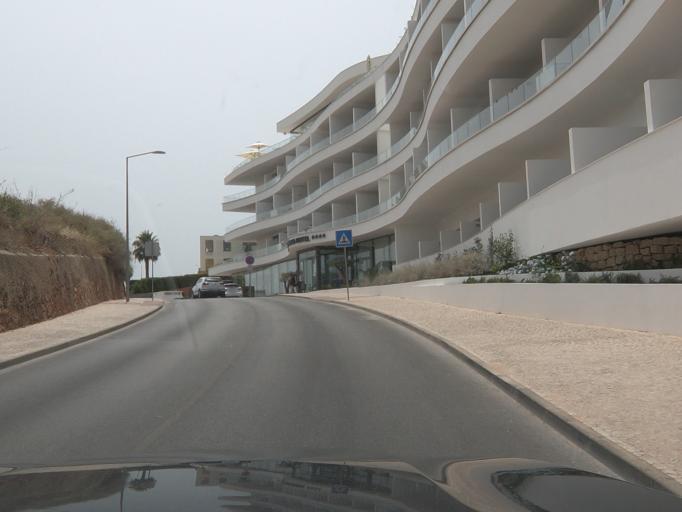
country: PT
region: Faro
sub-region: Portimao
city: Portimao
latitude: 37.1290
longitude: -8.5336
